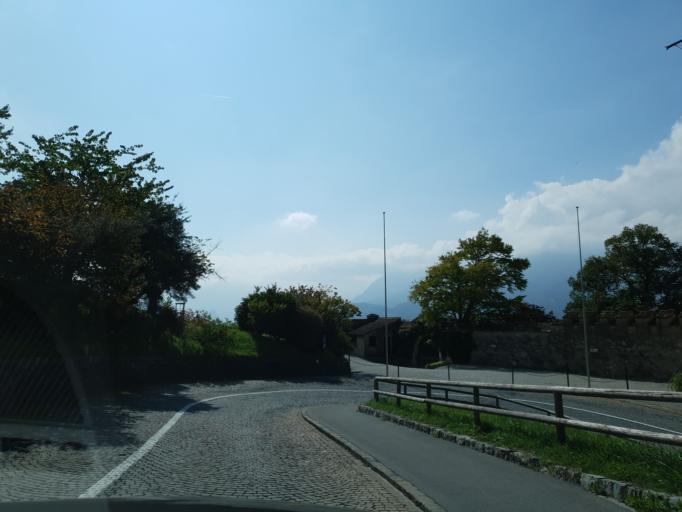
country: LI
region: Vaduz
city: Vaduz
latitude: 47.1394
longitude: 9.5251
